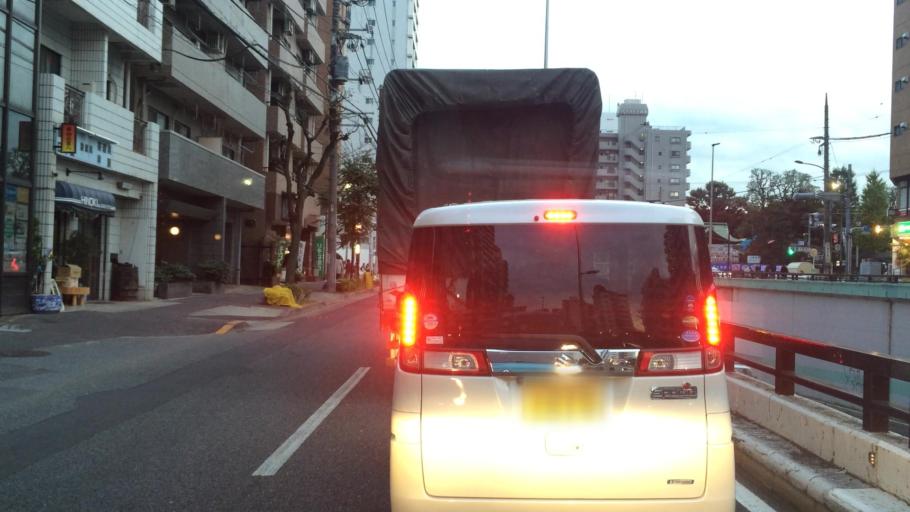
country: JP
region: Tokyo
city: Tokyo
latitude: 35.6334
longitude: 139.7079
